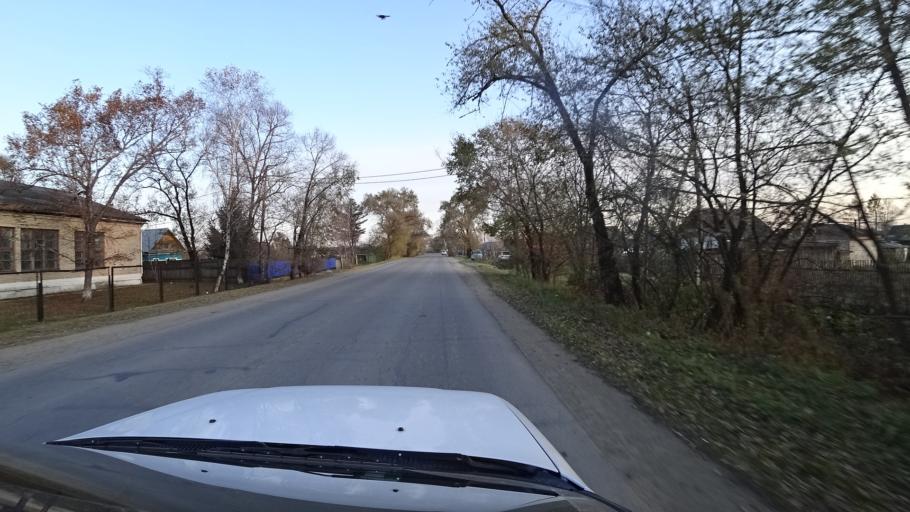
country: RU
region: Primorskiy
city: Dal'nerechensk
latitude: 45.9403
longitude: 133.8086
